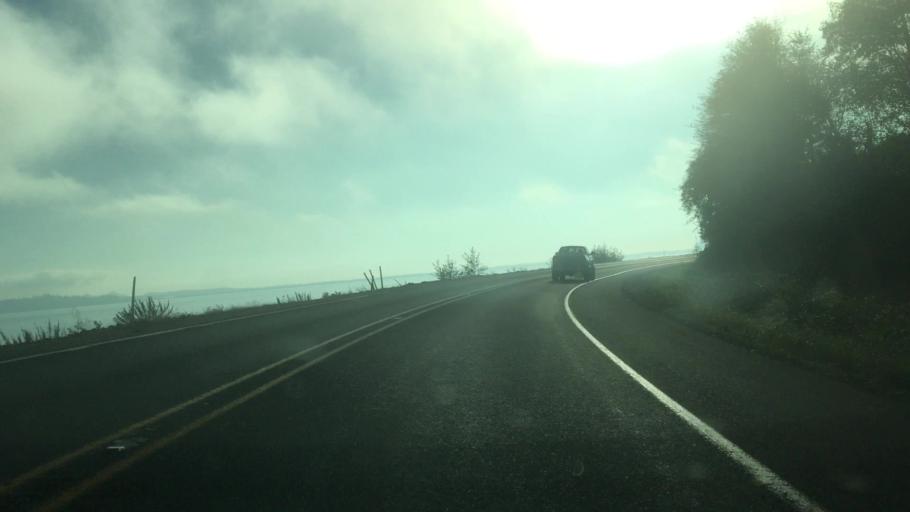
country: US
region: Oregon
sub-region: Clatsop County
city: Astoria
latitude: 46.2706
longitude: -123.8173
